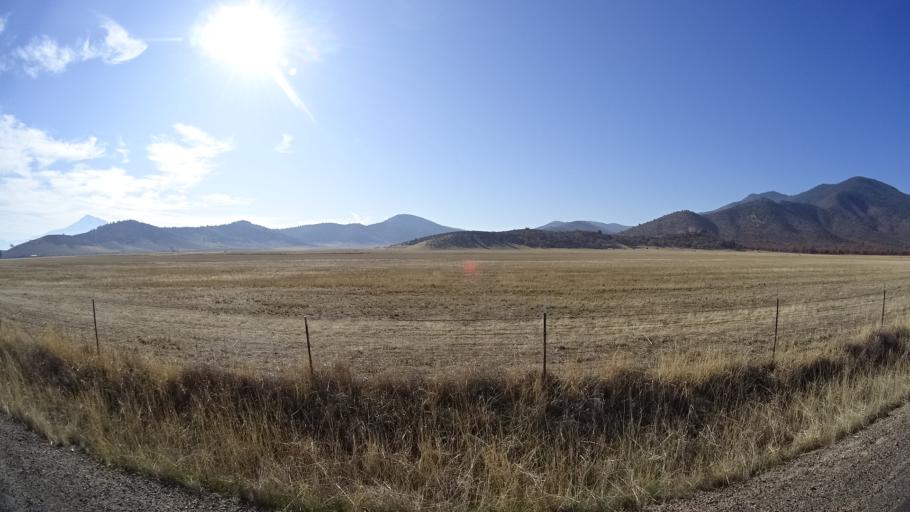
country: US
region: California
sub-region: Siskiyou County
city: Montague
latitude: 41.6549
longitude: -122.5703
